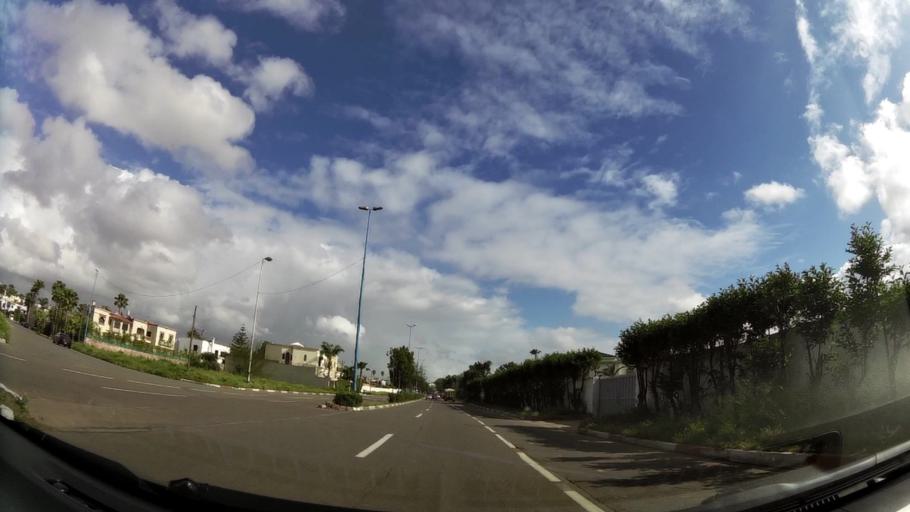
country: MA
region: Grand Casablanca
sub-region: Casablanca
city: Casablanca
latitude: 33.5446
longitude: -7.6208
